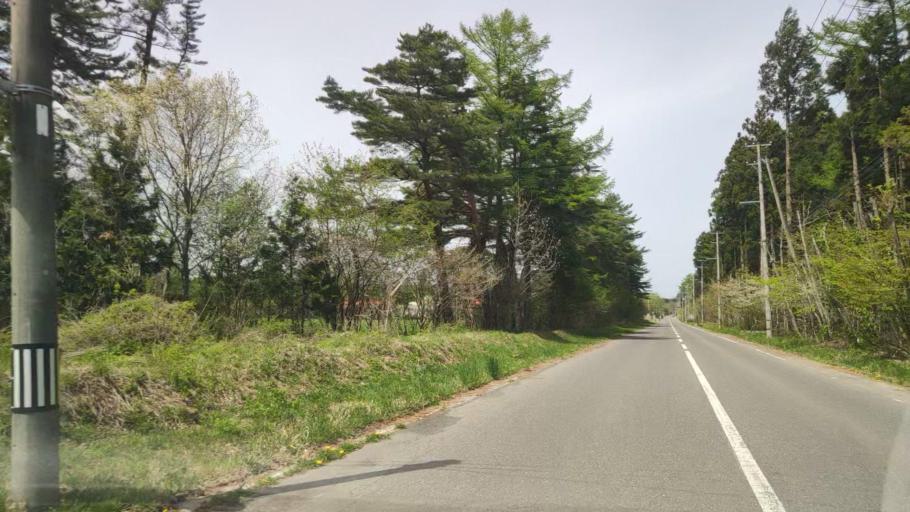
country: JP
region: Aomori
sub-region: Misawa Shi
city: Inuotose
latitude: 40.7153
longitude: 141.1438
